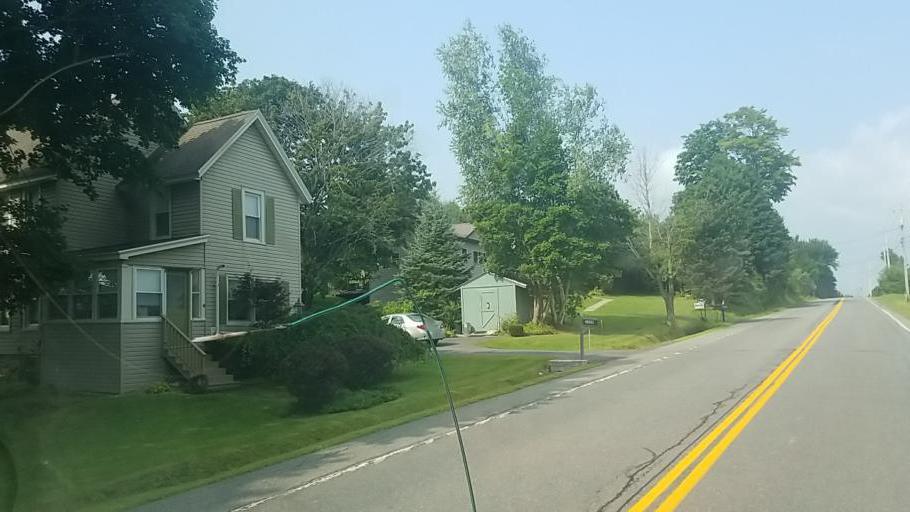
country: US
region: New York
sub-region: Fulton County
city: Johnstown
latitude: 43.0171
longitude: -74.3890
